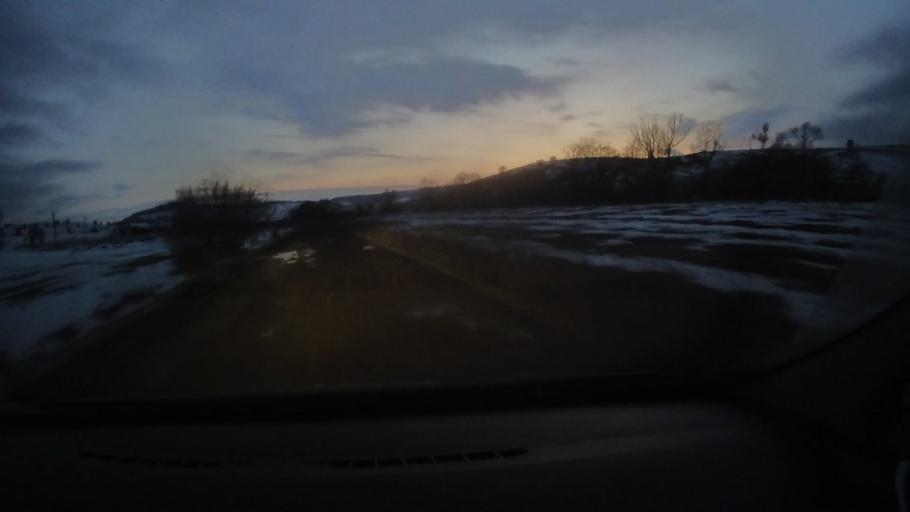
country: RO
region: Harghita
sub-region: Comuna Darjiu
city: Darjiu
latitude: 46.1573
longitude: 25.2035
